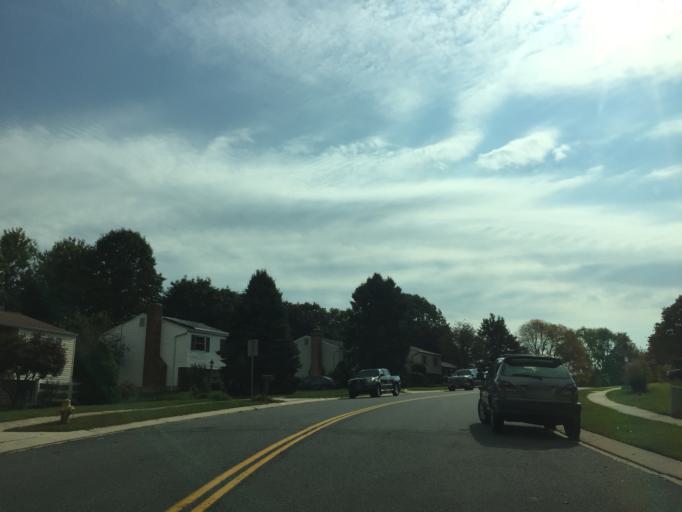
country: US
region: Maryland
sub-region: Harford County
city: Bel Air South
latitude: 39.4839
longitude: -76.3000
